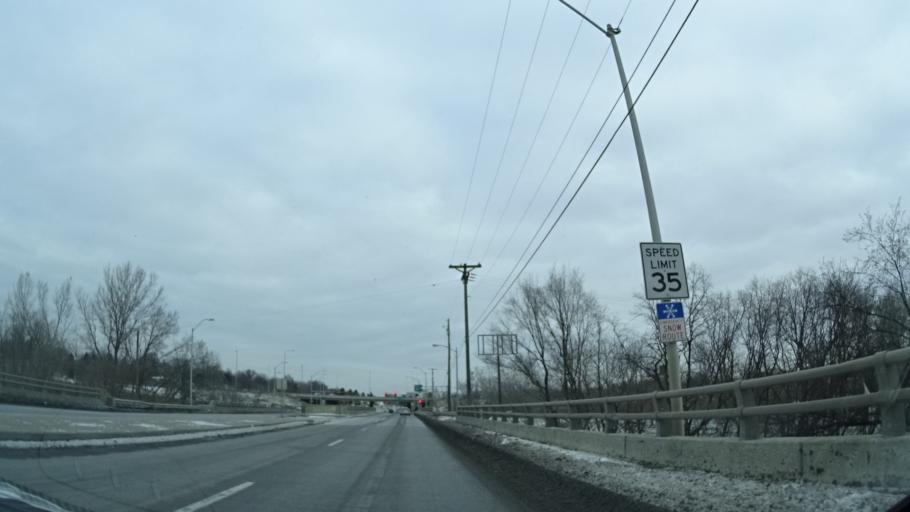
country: US
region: Nebraska
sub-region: Douglas County
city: Omaha
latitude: 41.2220
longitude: -95.9757
